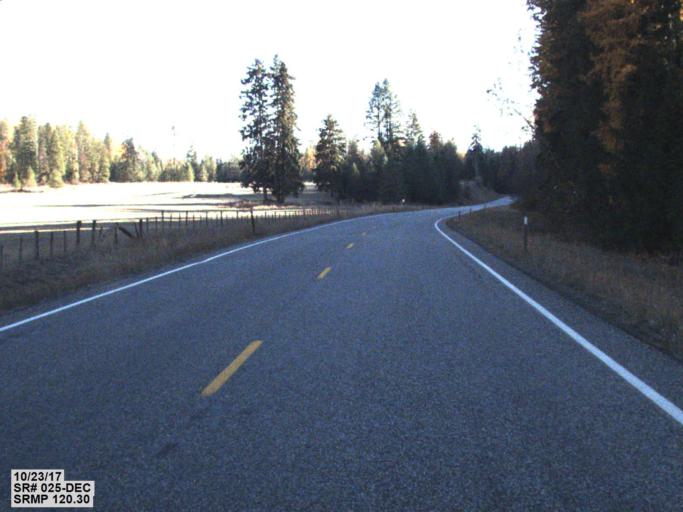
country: CA
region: British Columbia
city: Rossland
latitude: 48.9876
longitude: -117.8278
